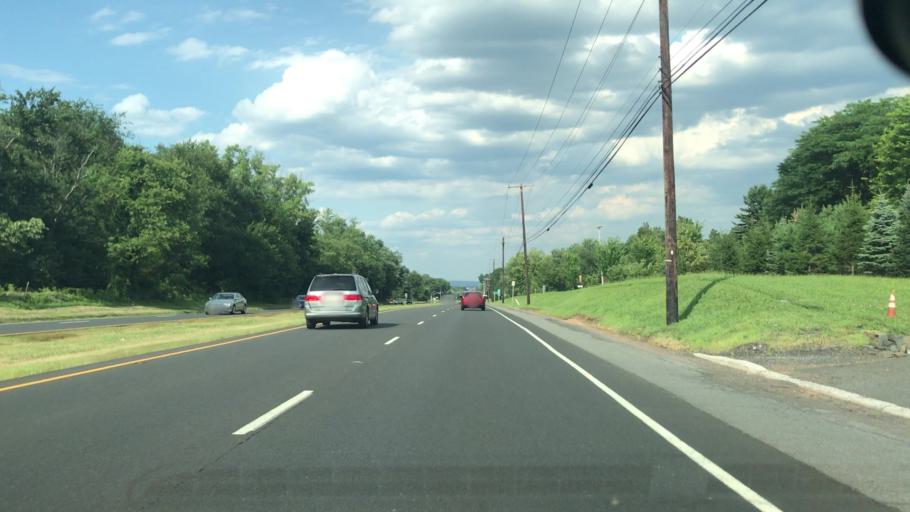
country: US
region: New Jersey
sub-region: Hunterdon County
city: Whitehouse Station
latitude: 40.5458
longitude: -74.7446
